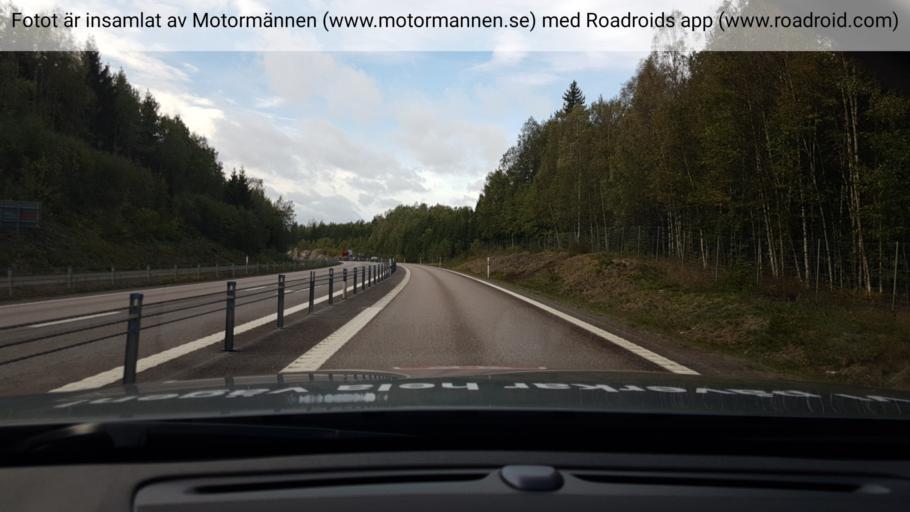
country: SE
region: Vaermland
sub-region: Karlstads Kommun
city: Valberg
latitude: 59.3711
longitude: 13.1638
